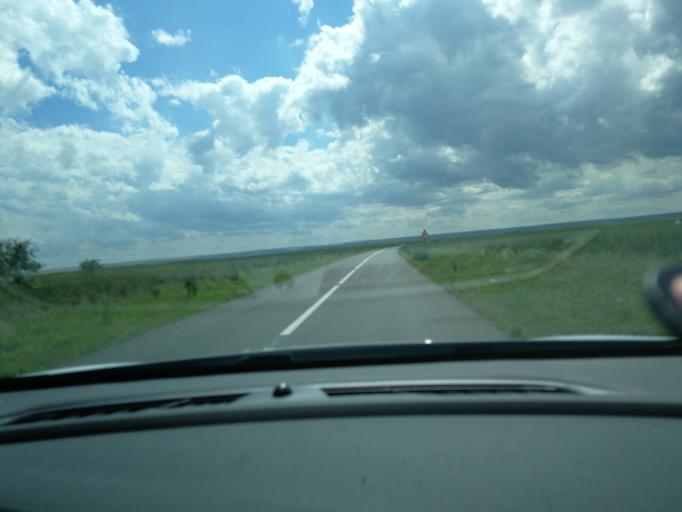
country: RO
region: Constanta
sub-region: Comuna Istria
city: Istria
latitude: 44.5393
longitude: 28.7562
